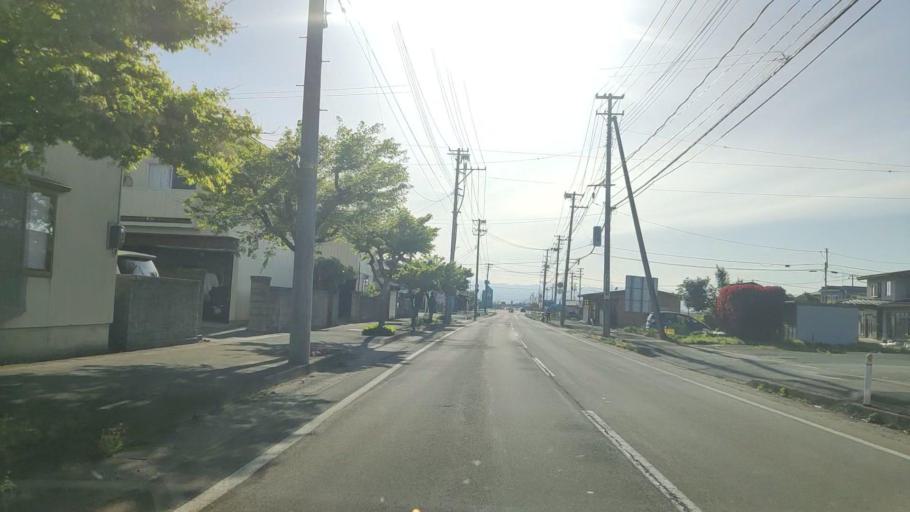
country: JP
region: Yamagata
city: Tendo
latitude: 38.3659
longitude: 140.3637
